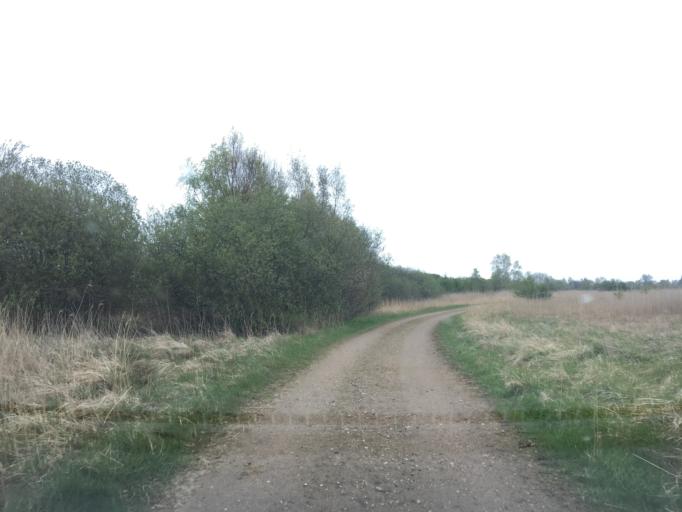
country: DK
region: Capital Region
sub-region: Tarnby Kommune
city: Tarnby
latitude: 55.5849
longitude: 12.5681
